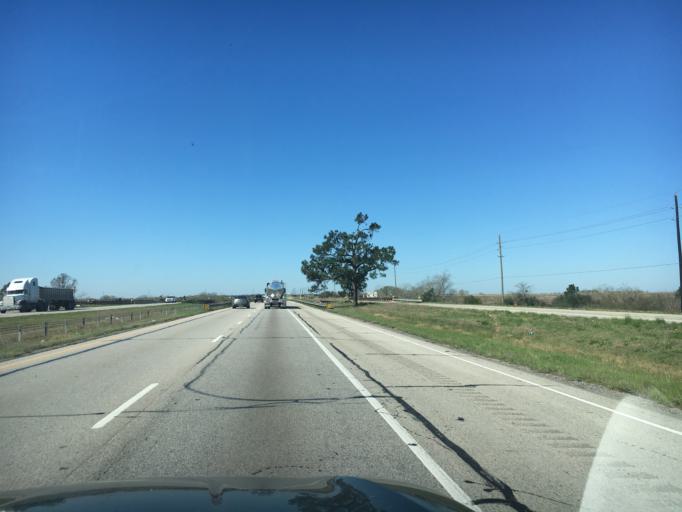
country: US
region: Texas
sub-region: Austin County
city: Sealy
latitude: 29.7542
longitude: -96.2570
